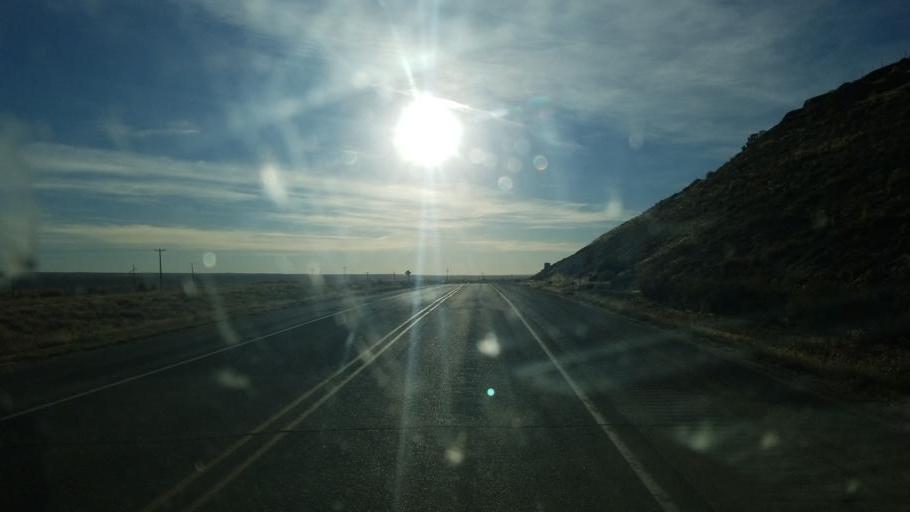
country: US
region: New Mexico
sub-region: San Juan County
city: Bloomfield
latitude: 36.7134
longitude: -107.8425
